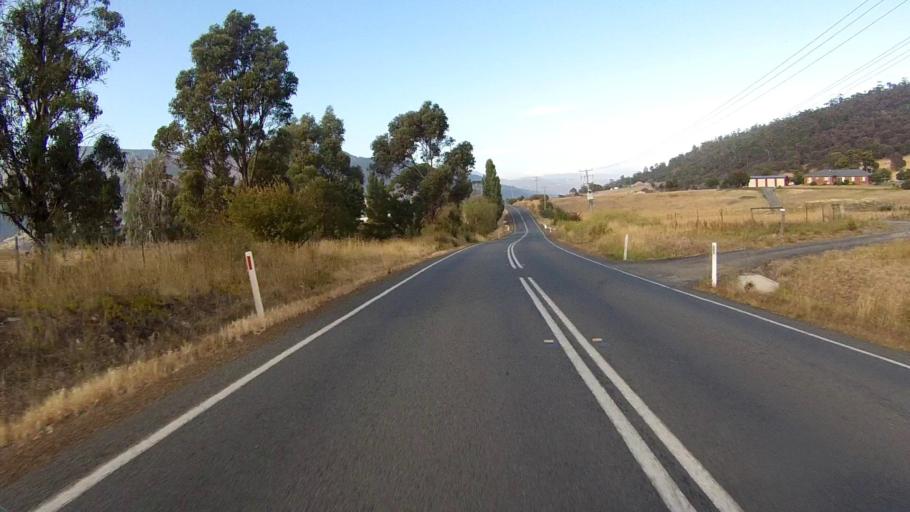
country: AU
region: Tasmania
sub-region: Brighton
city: Bridgewater
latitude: -42.7343
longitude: 147.1756
